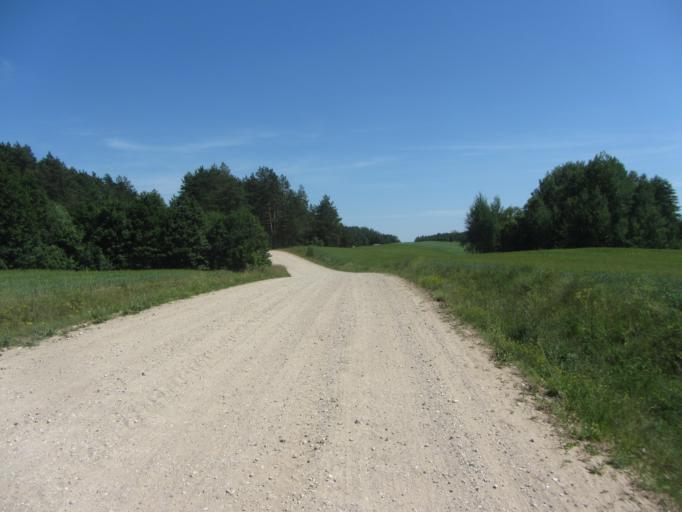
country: LT
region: Alytaus apskritis
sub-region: Alytaus rajonas
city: Daugai
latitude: 54.2939
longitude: 24.2611
